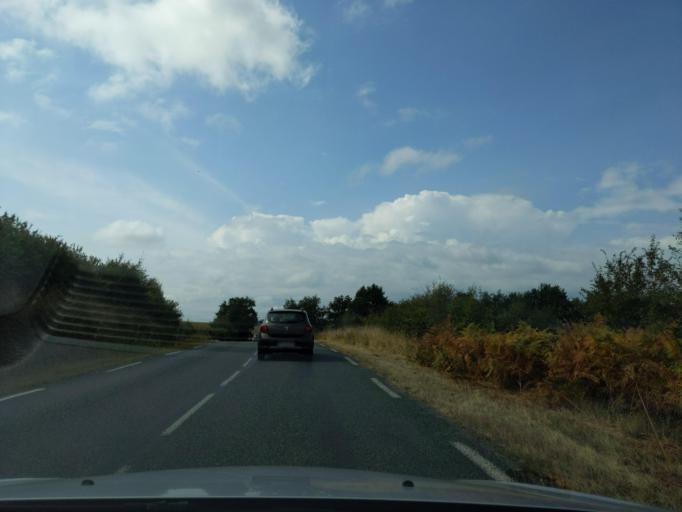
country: FR
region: Bourgogne
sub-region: Departement de Saone-et-Loire
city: Bourbon-Lancy
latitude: 46.6622
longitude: 3.7999
